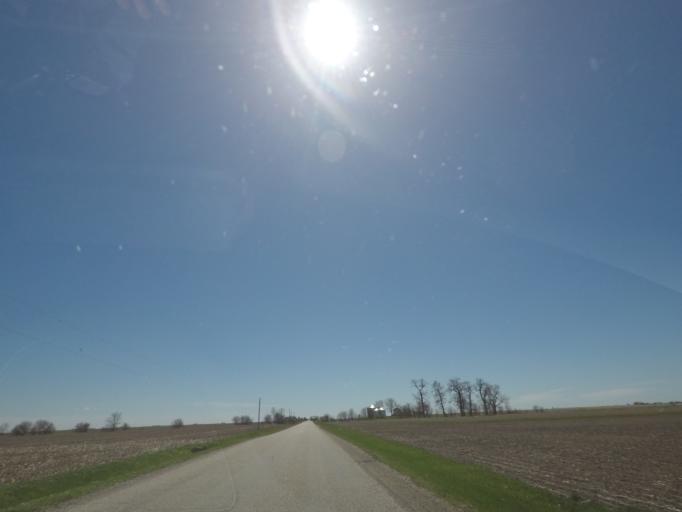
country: US
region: Illinois
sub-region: Logan County
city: Atlanta
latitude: 40.1980
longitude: -89.1942
